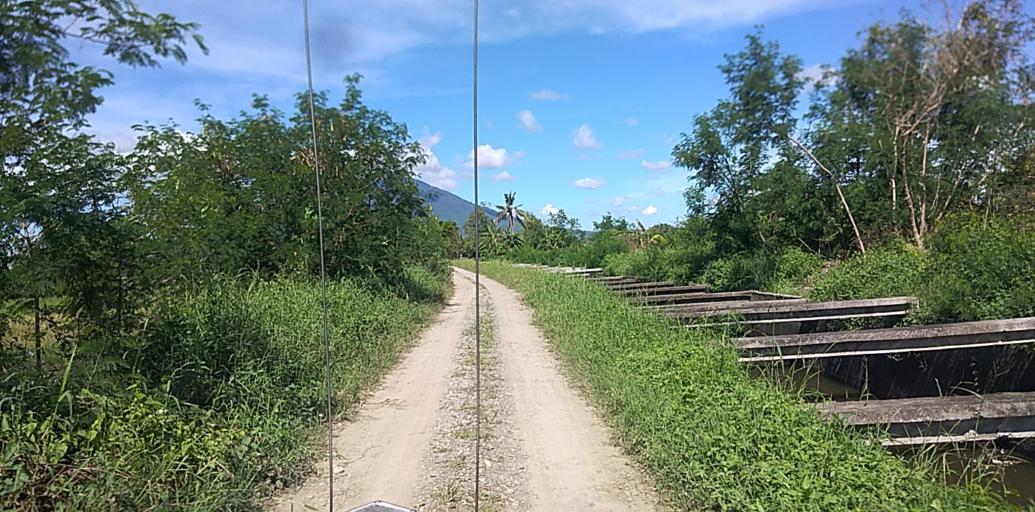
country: PH
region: Central Luzon
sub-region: Province of Pampanga
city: Candating
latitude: 15.1289
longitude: 120.7982
